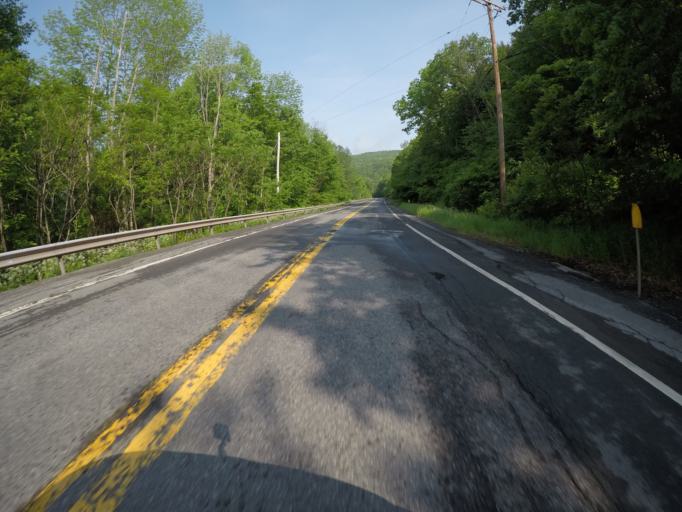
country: US
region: New York
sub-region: Sullivan County
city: Livingston Manor
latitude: 42.1249
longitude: -74.7054
